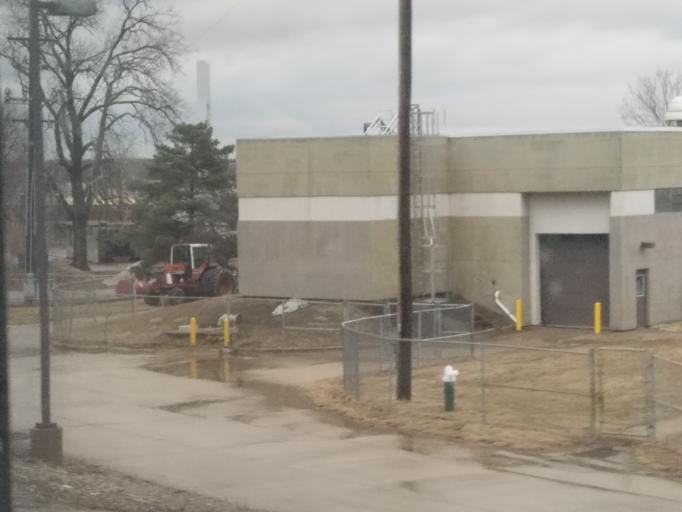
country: US
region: Iowa
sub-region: Des Moines County
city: Burlington
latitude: 40.7988
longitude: -91.0988
